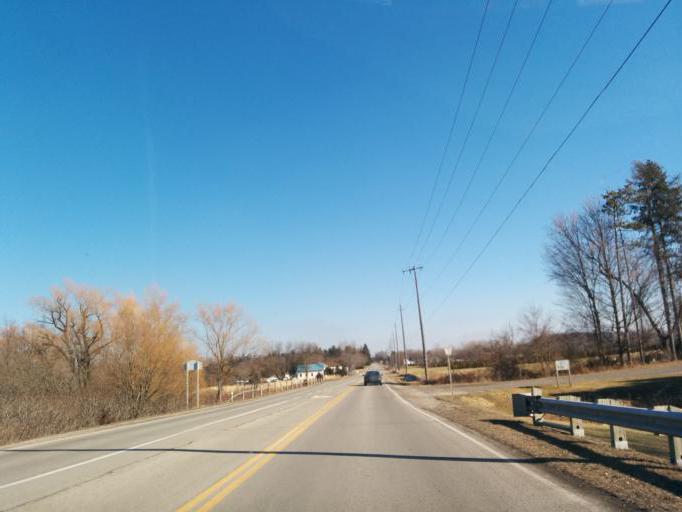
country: CA
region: Ontario
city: Norfolk County
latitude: 42.8294
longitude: -80.3354
